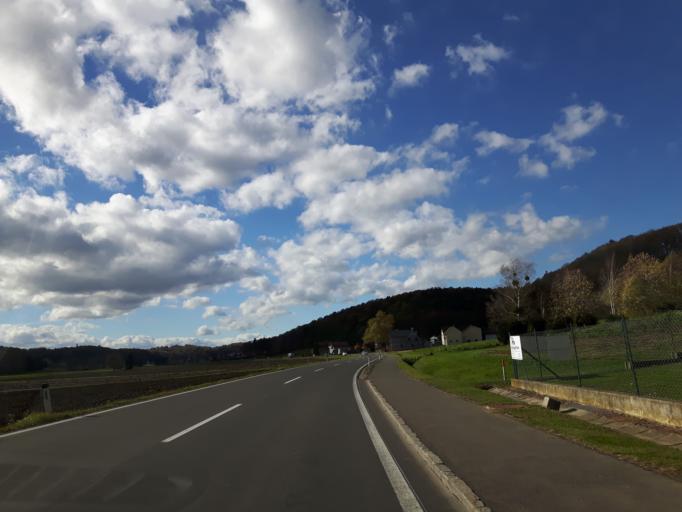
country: AT
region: Styria
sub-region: Politischer Bezirk Suedoststeiermark
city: Oberstorcha
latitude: 46.9508
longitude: 15.8210
